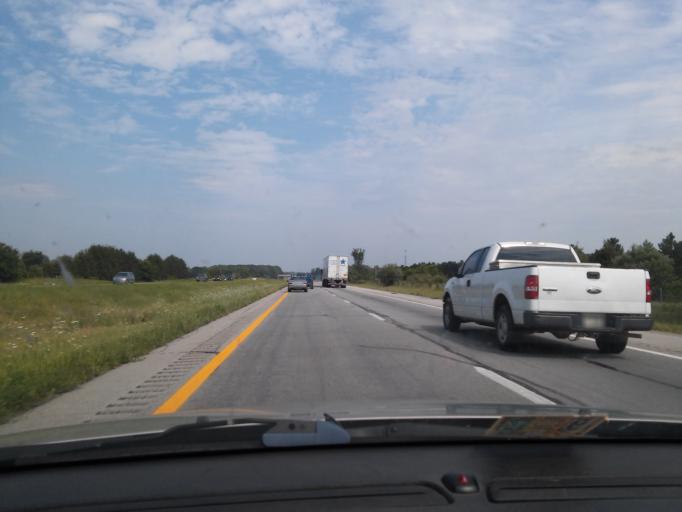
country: US
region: Ohio
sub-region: Montgomery County
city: Brookville
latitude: 39.8569
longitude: -84.4011
